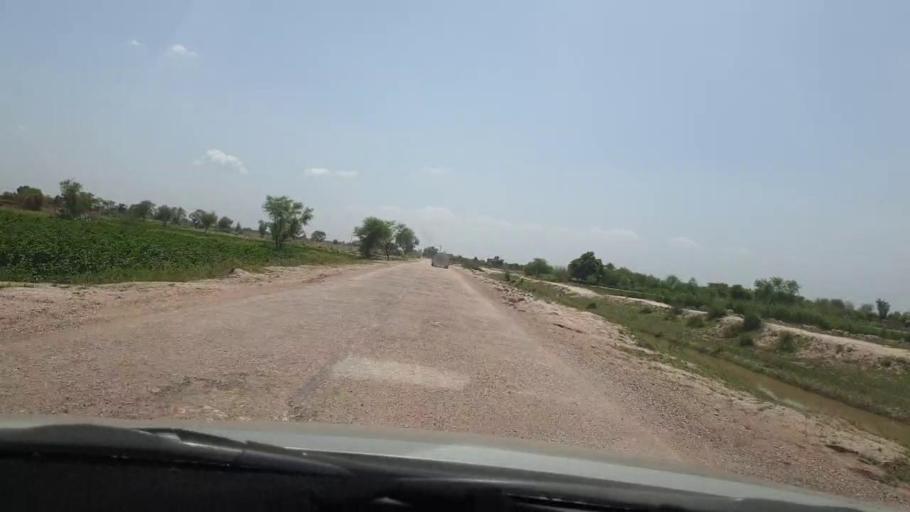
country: PK
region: Sindh
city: Pano Aqil
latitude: 27.7220
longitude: 69.1757
